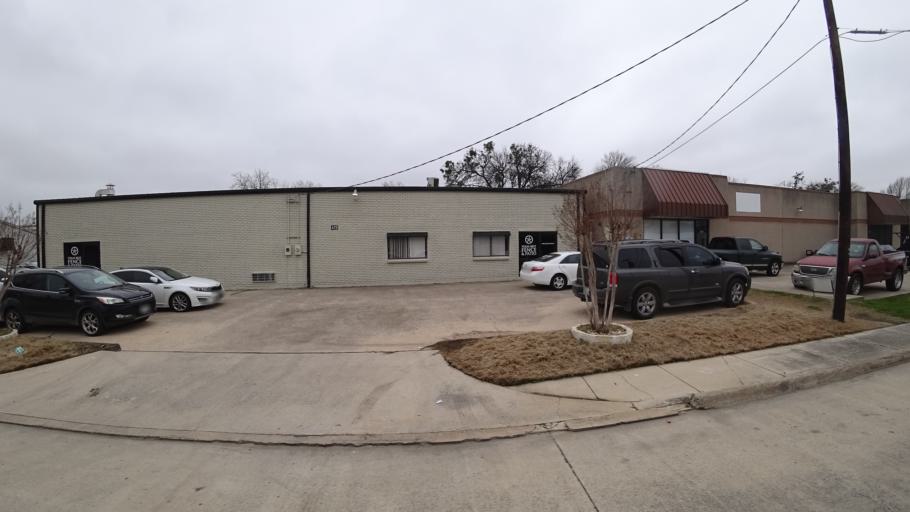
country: US
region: Texas
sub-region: Denton County
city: Lewisville
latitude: 33.0557
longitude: -97.0029
